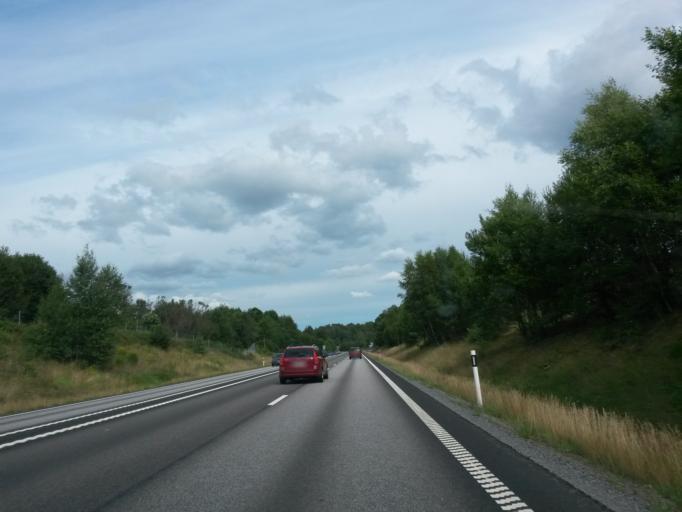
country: SE
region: Vaestra Goetaland
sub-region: Marks Kommun
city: Kinna
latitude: 57.4840
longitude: 12.6701
